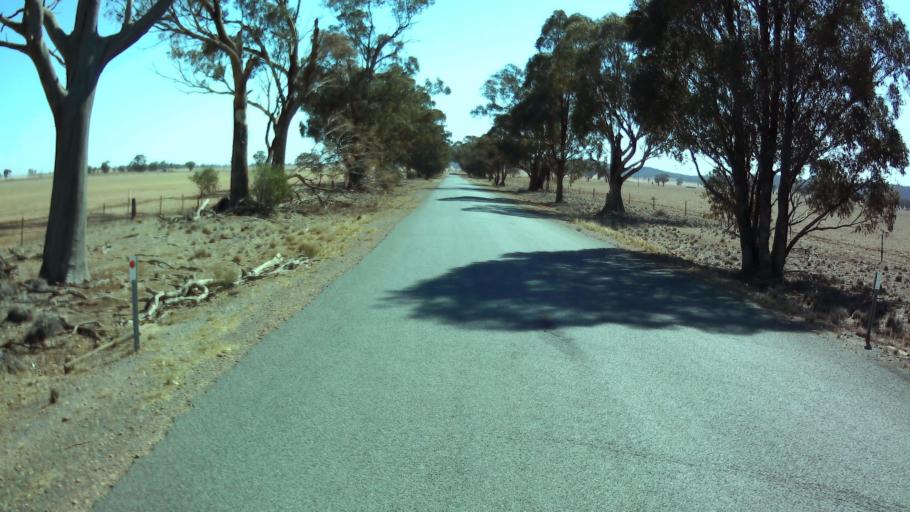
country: AU
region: New South Wales
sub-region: Weddin
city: Grenfell
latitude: -33.7089
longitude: 147.9139
